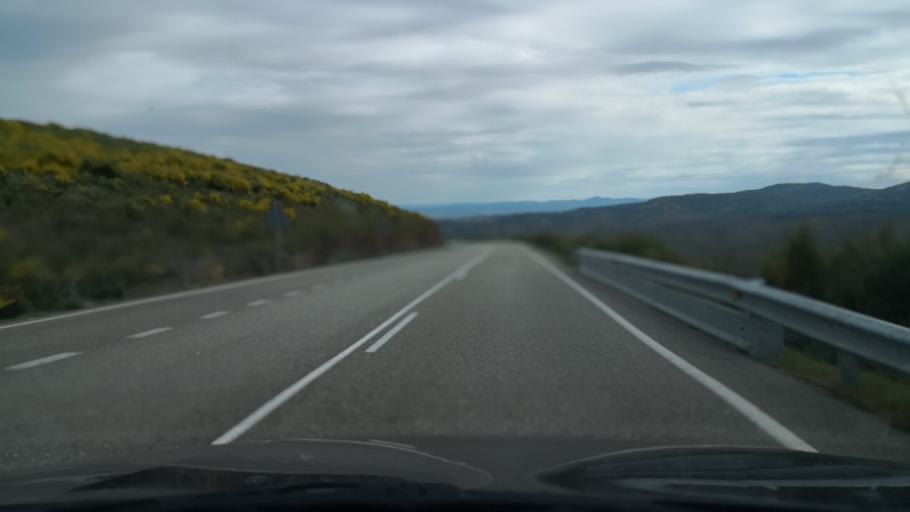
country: ES
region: Extremadura
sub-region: Provincia de Caceres
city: Acebo
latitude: 40.2117
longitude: -6.6764
